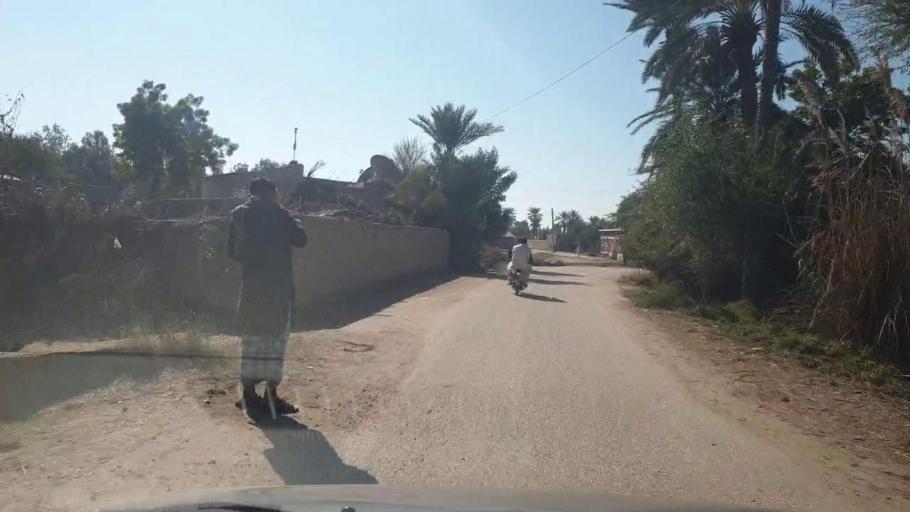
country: PK
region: Sindh
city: Bozdar
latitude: 27.1369
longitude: 68.6446
